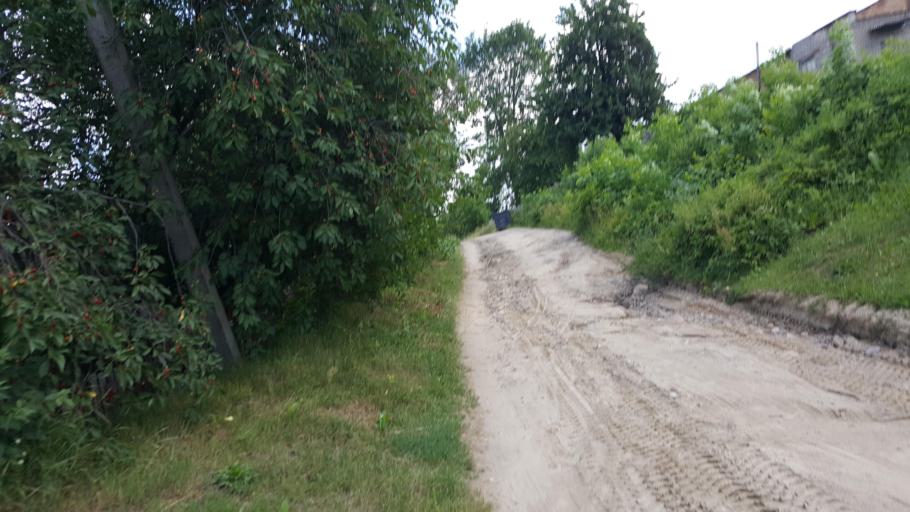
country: BY
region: Brest
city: Kamyanyets
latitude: 52.4044
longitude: 23.8309
